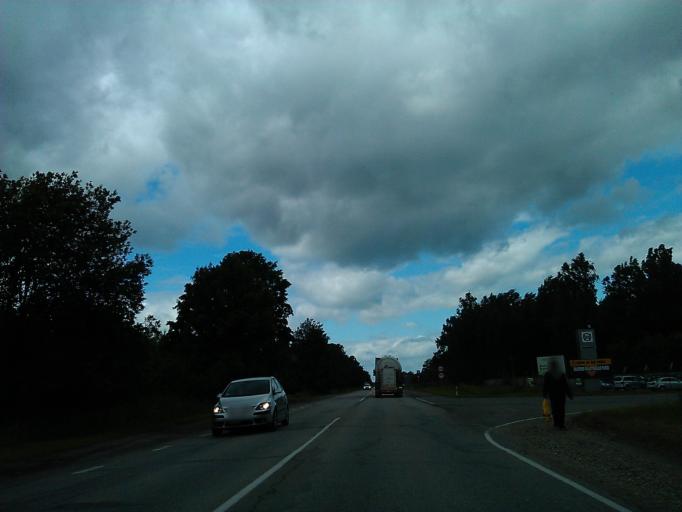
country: LV
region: Tukuma Rajons
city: Tukums
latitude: 56.9305
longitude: 23.2117
